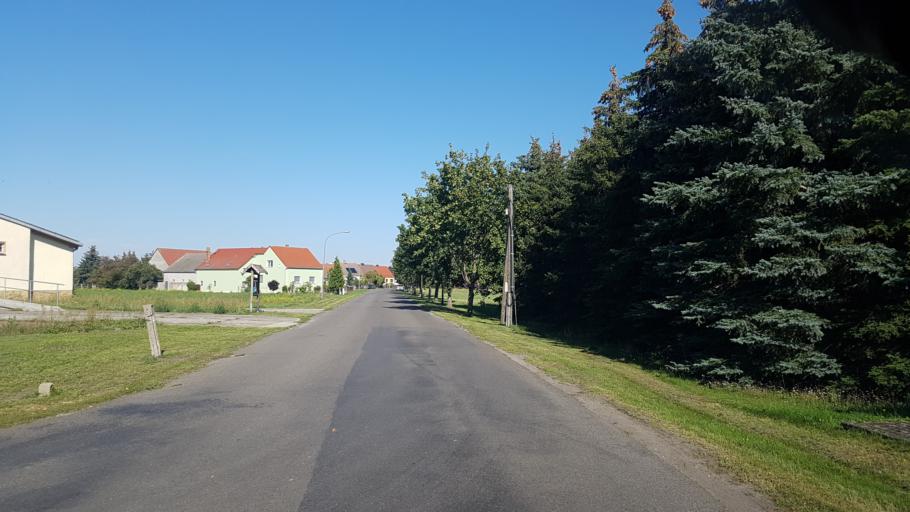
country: DE
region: Brandenburg
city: Schraden
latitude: 51.4251
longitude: 13.6948
